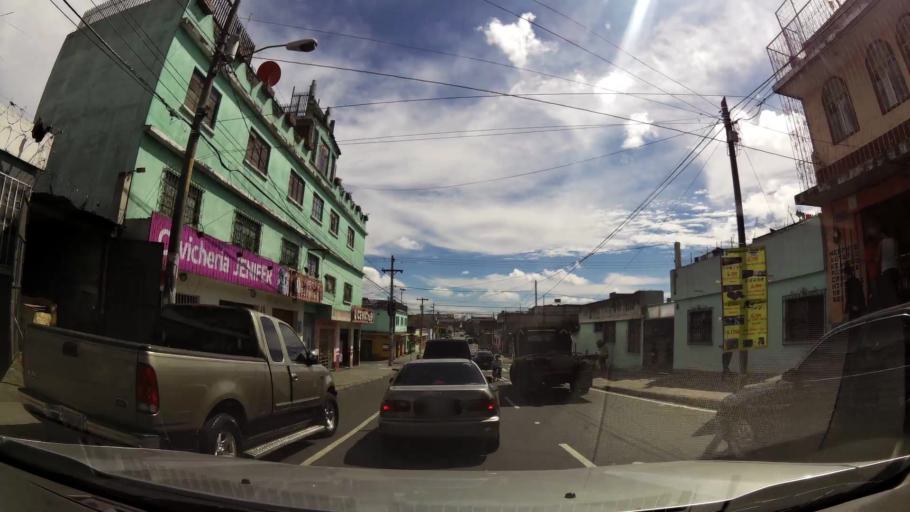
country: GT
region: Guatemala
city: Mixco
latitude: 14.6529
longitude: -90.5841
